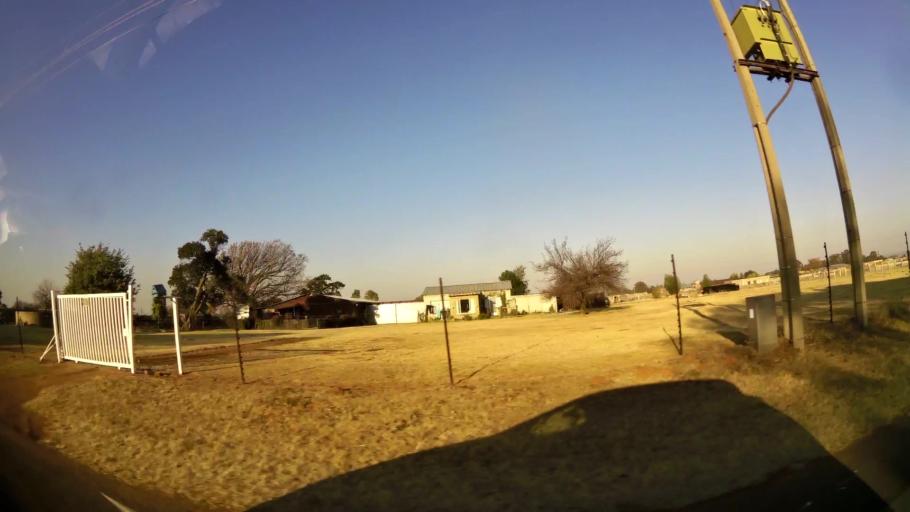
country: ZA
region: Gauteng
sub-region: West Rand District Municipality
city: Randfontein
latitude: -26.2055
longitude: 27.6445
